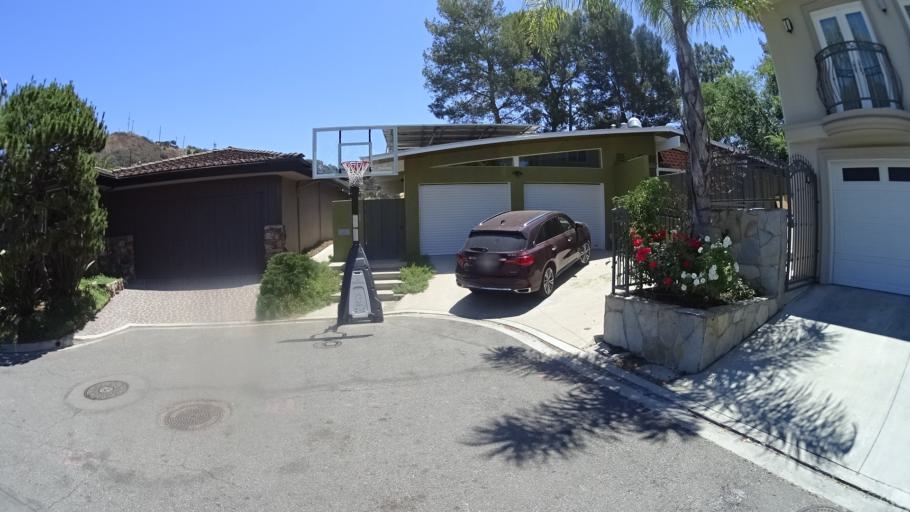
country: US
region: California
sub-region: Los Angeles County
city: Universal City
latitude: 34.1237
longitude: -118.3720
